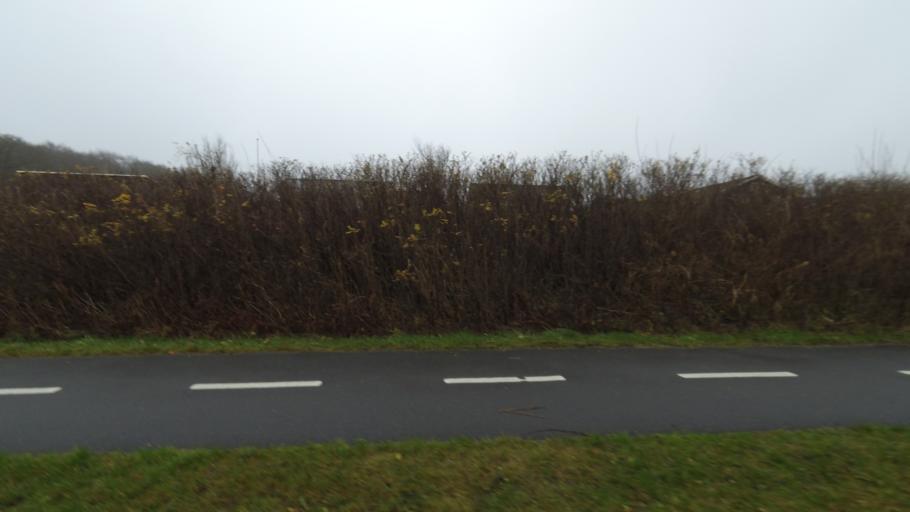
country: DK
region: Central Jutland
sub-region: Arhus Kommune
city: Stavtrup
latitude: 56.1435
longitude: 10.1113
